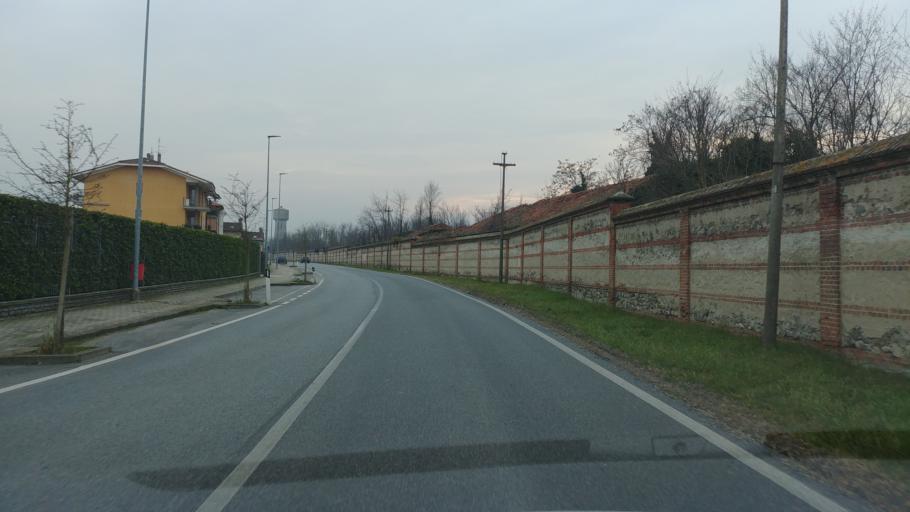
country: IT
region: Piedmont
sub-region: Provincia di Cuneo
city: Fossano
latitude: 44.5338
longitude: 7.7110
